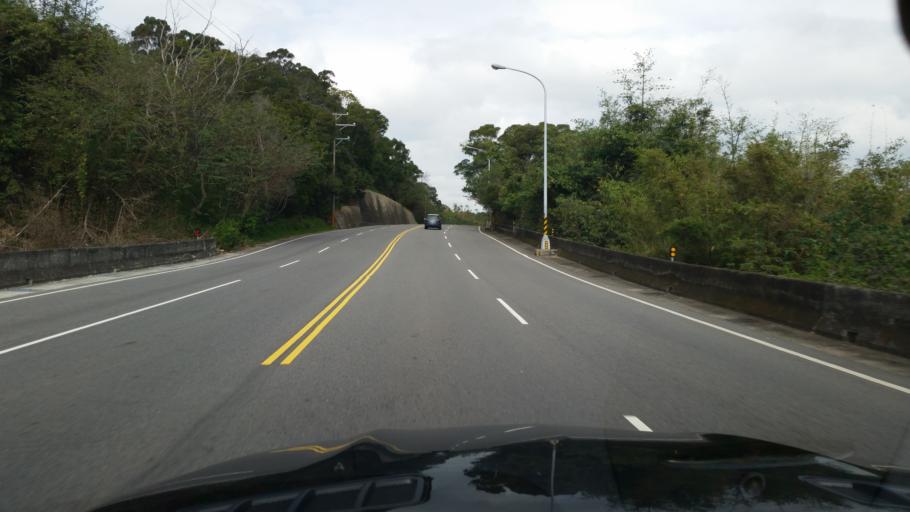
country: TW
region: Taiwan
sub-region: Miaoli
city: Miaoli
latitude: 24.6466
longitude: 120.8613
